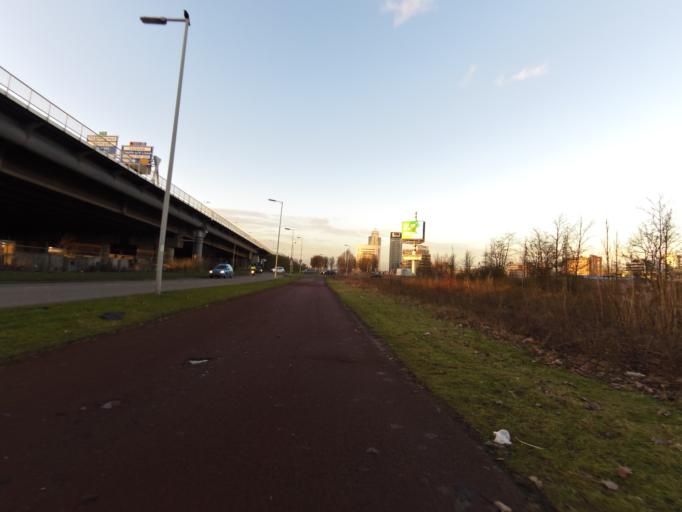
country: NL
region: South Holland
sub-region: Gemeente Rotterdam
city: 's-Gravenland
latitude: 51.9084
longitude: 4.5405
